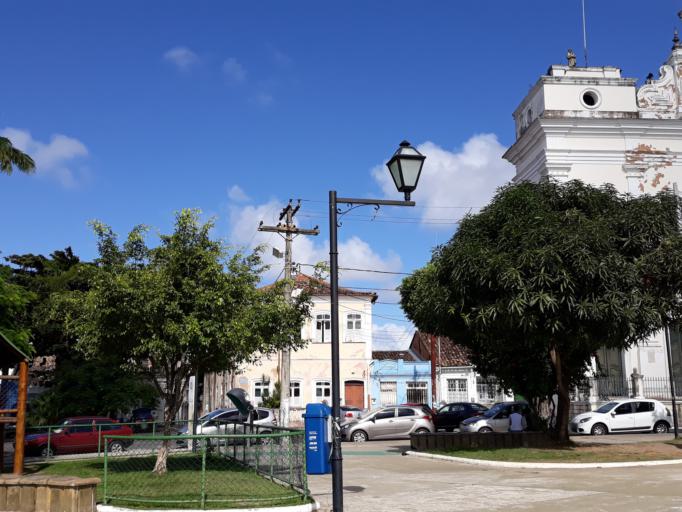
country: BR
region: Bahia
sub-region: Salvador
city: Salvador
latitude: -12.9631
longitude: -38.5035
